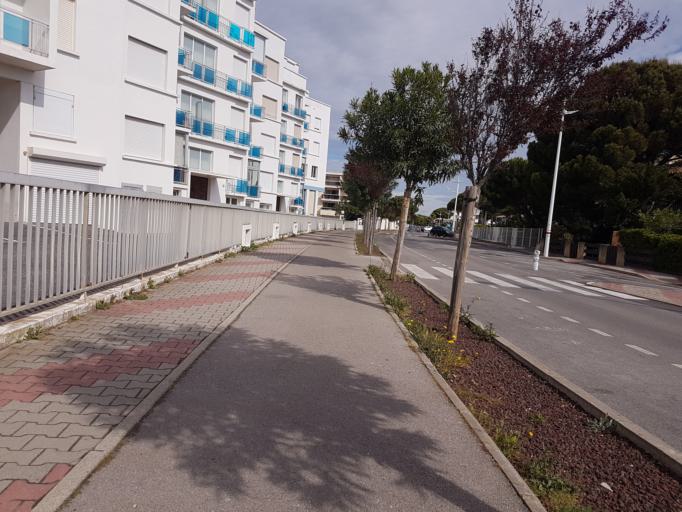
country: FR
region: Languedoc-Roussillon
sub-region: Departement du Gard
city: Le Grau-du-Roi
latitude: 43.5469
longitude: 4.1240
